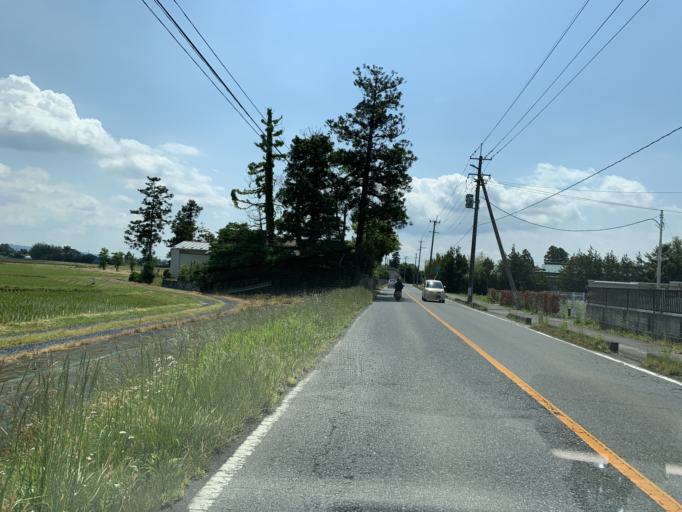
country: JP
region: Miyagi
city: Kogota
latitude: 38.5748
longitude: 141.0354
